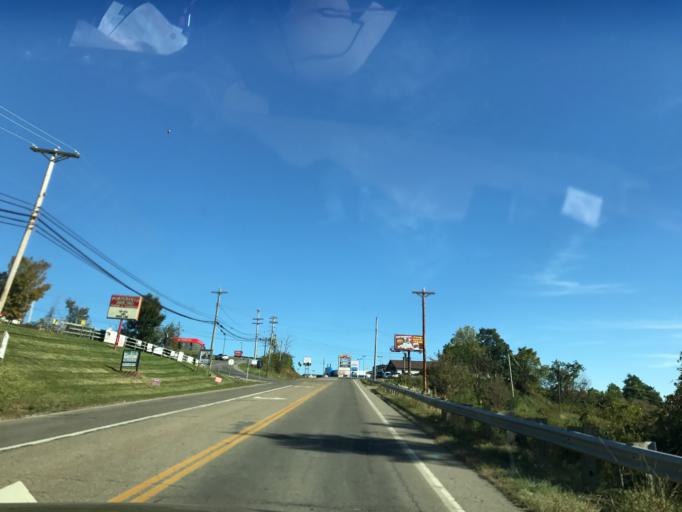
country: US
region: Ohio
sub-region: Belmont County
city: Saint Clairsville
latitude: 40.0788
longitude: -80.8752
